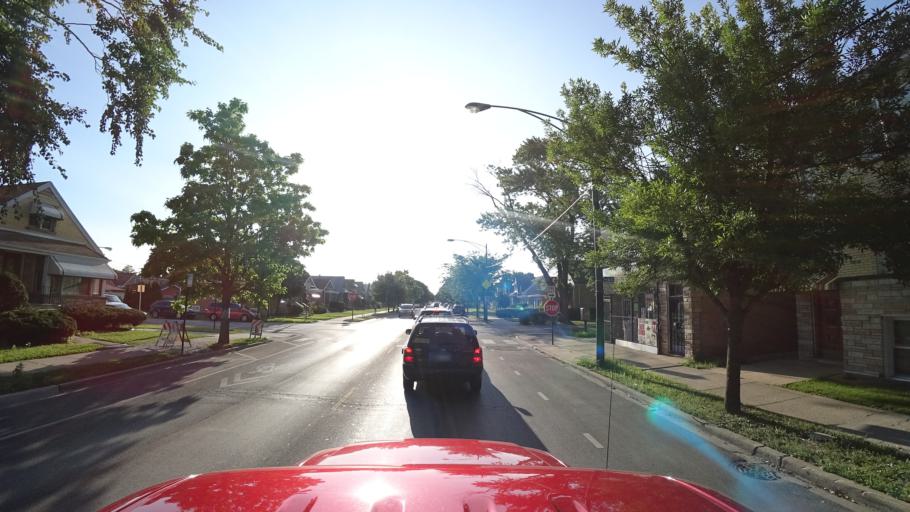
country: US
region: Illinois
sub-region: Cook County
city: Hometown
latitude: 41.7859
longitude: -87.7282
